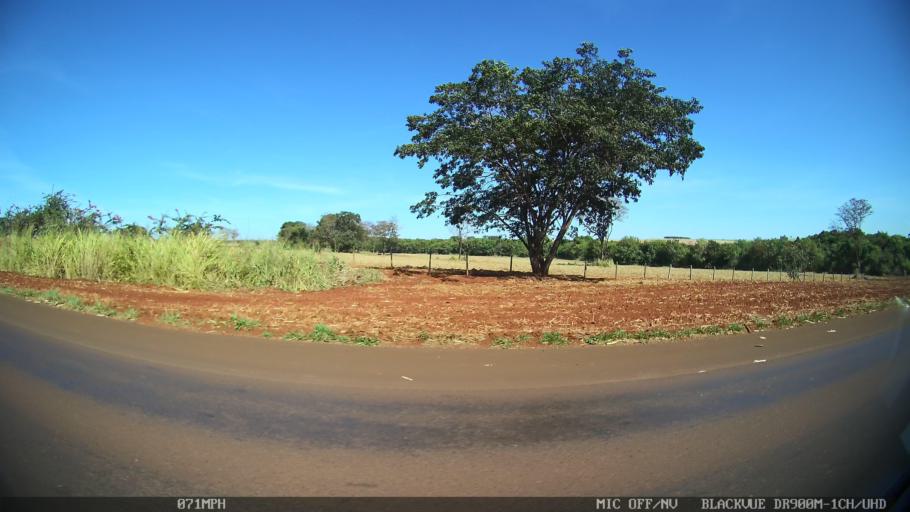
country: BR
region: Sao Paulo
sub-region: Ipua
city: Ipua
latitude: -20.4931
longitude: -47.9856
